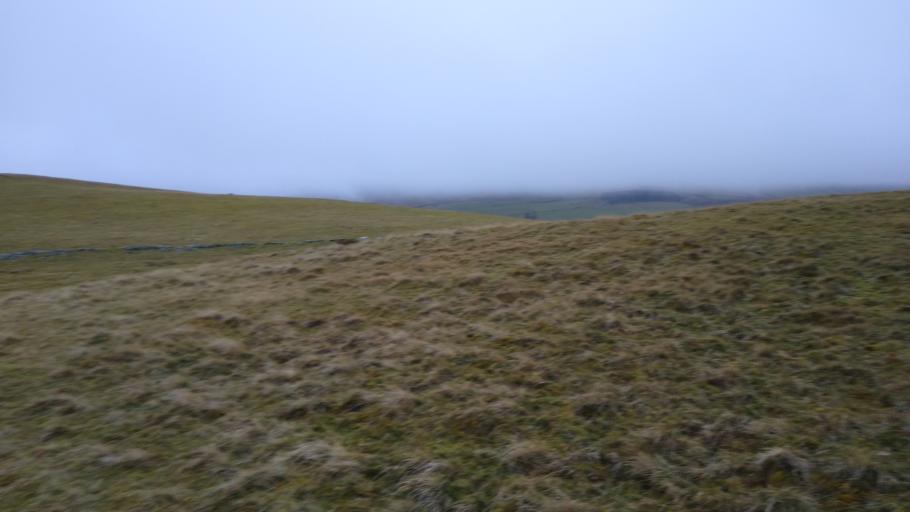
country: GB
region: England
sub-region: Cumbria
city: Cockermouth
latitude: 54.6550
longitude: -3.2467
